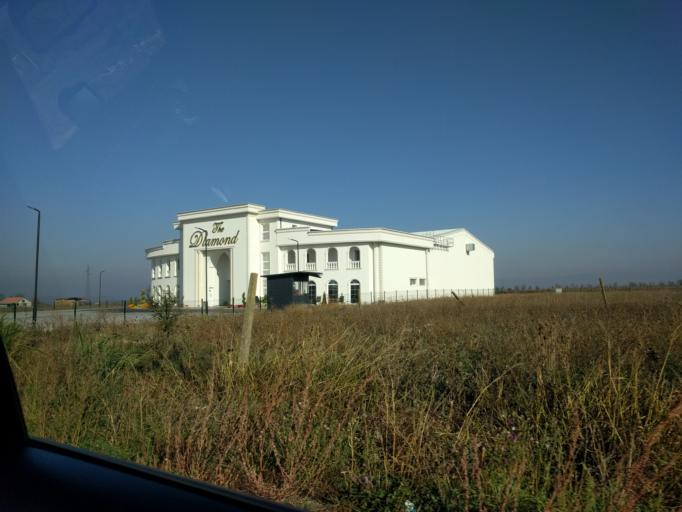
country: XK
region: Prizren
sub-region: Prizren
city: Prizren
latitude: 42.2436
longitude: 20.7476
